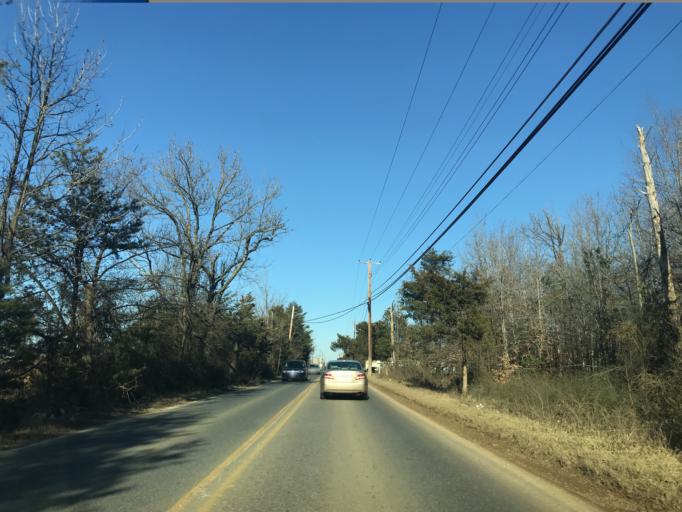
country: US
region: Maryland
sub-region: Prince George's County
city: Friendly
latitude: 38.7436
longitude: -76.9365
